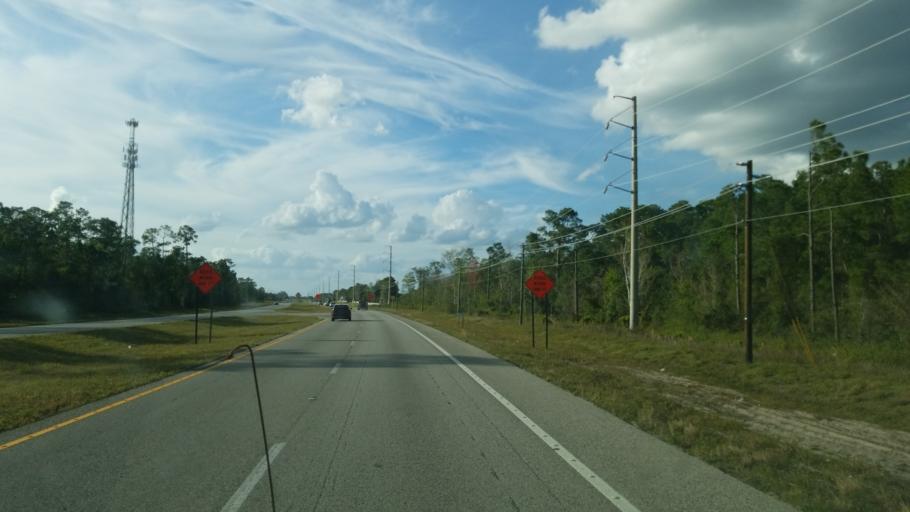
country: US
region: Florida
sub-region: Osceola County
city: Saint Cloud
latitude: 28.1838
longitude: -81.1388
